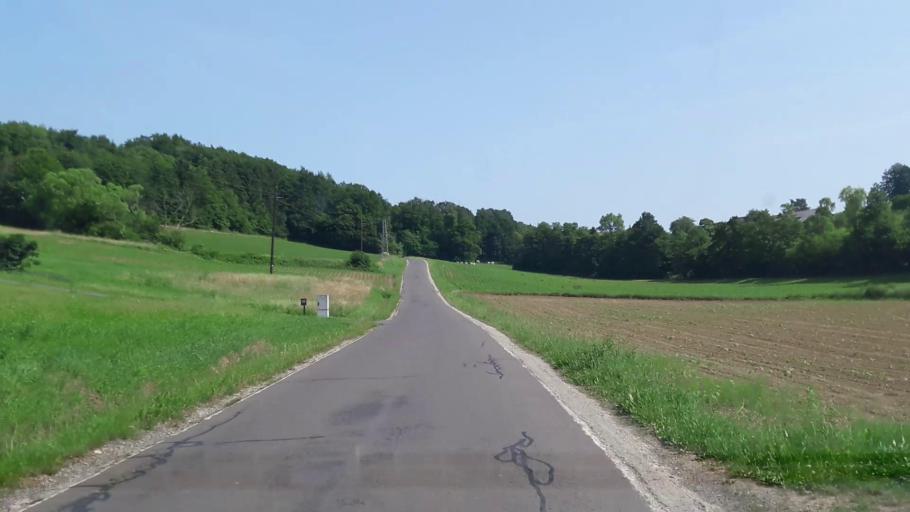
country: AT
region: Styria
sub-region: Politischer Bezirk Hartberg-Fuerstenfeld
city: UEbersbach
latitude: 46.9981
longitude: 16.0443
